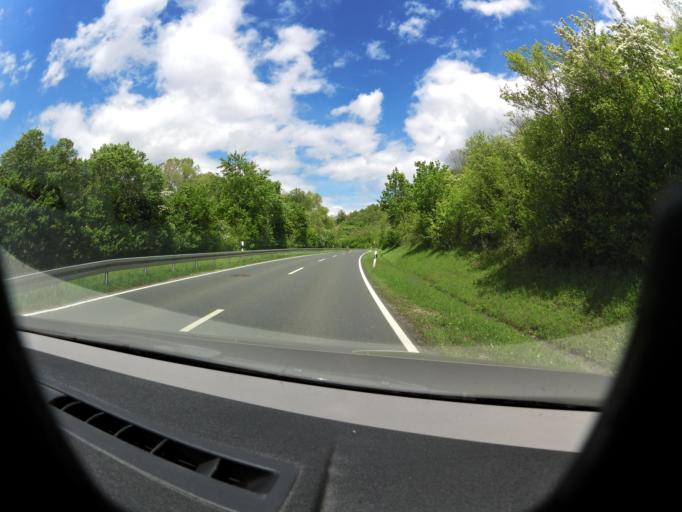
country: DE
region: Bavaria
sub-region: Regierungsbezirk Unterfranken
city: Frickenhausen
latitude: 49.6724
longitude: 10.0792
